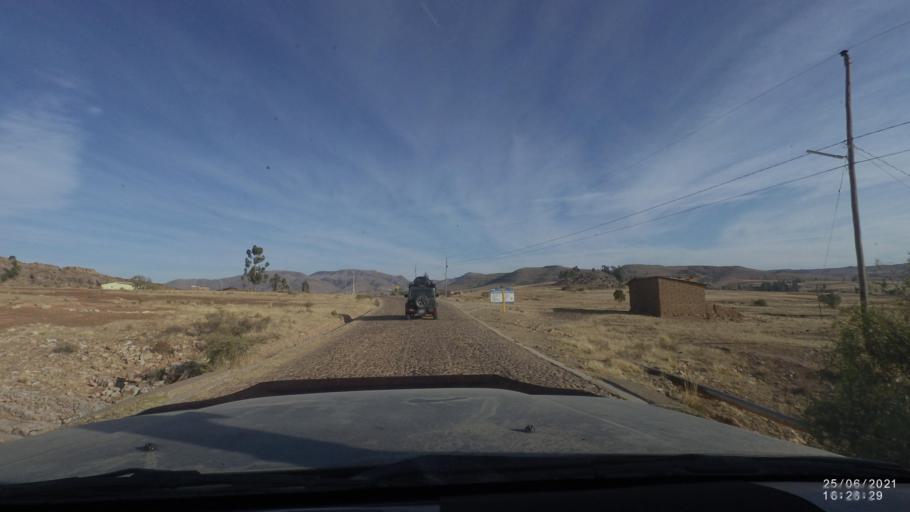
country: BO
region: Cochabamba
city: Arani
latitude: -17.7790
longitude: -65.8138
